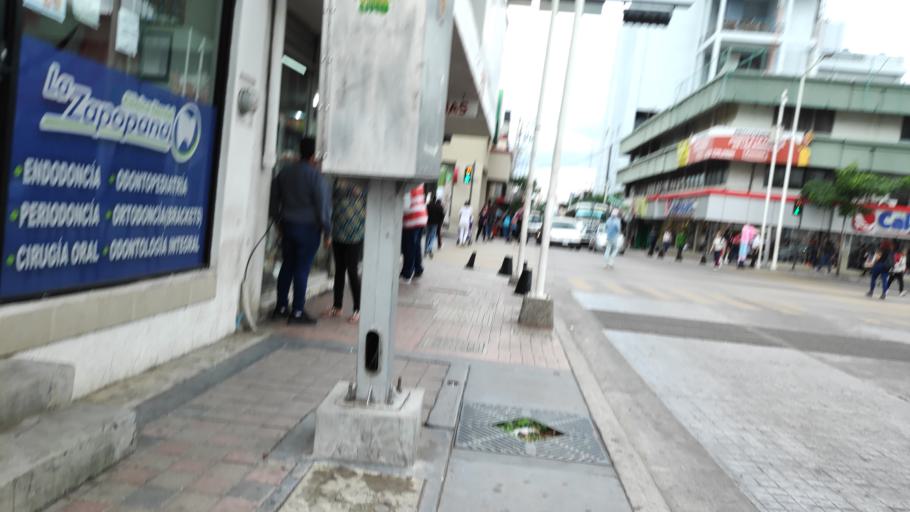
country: MX
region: Sinaloa
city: Culiacan
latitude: 24.8066
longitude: -107.3941
